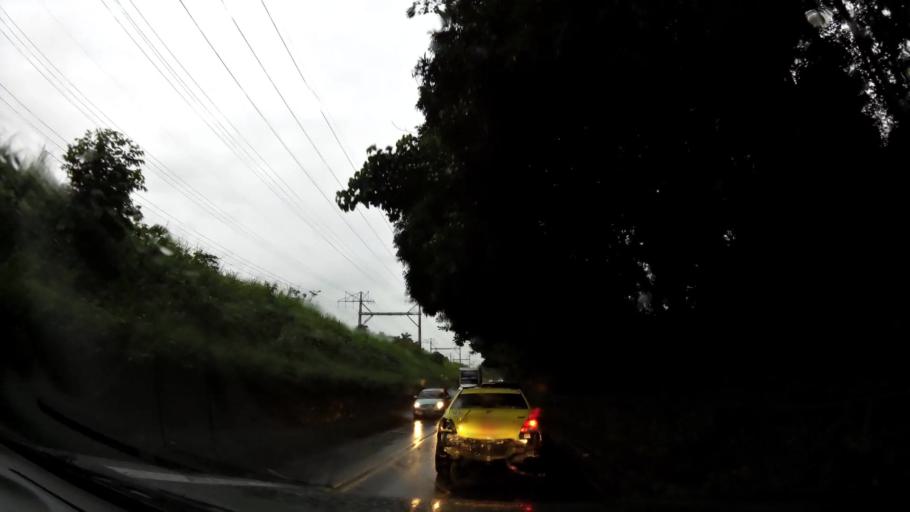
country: PA
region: Panama
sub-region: Distrito de Panama
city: Paraiso
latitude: 9.0163
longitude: -79.6064
